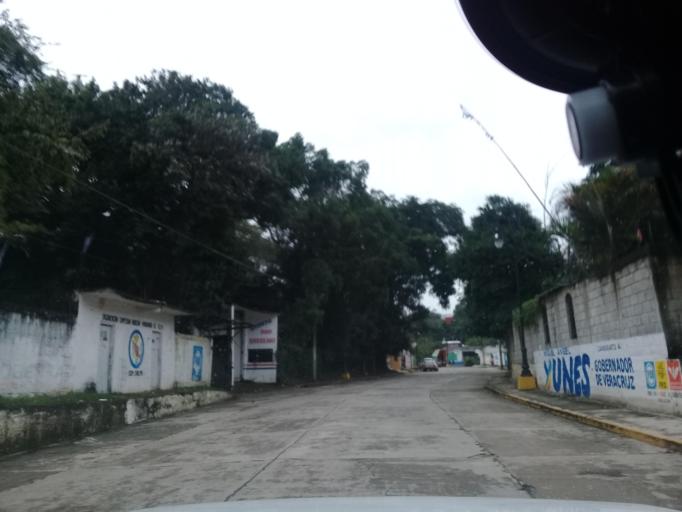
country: MX
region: Veracruz
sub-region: Chalma
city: San Pedro Coyutla
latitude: 21.2074
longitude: -98.3931
